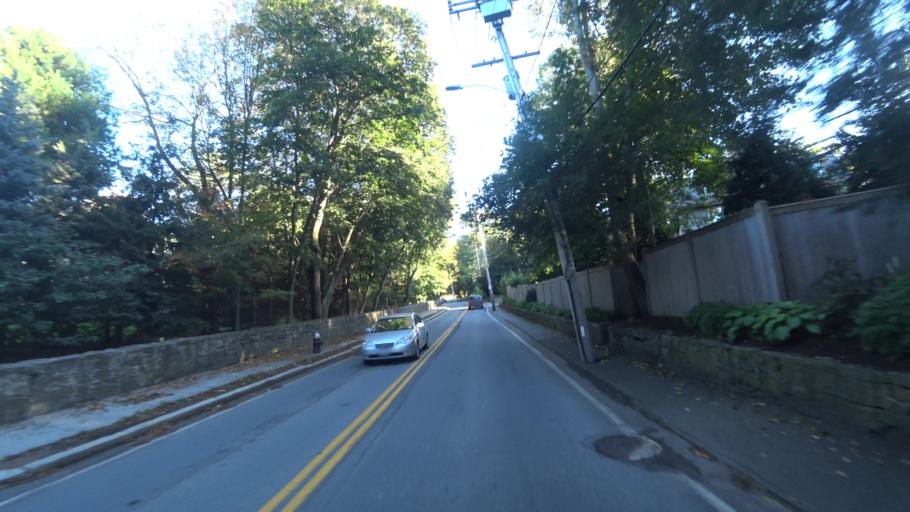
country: US
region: Massachusetts
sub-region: Norfolk County
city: Brookline
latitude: 42.3282
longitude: -71.1325
